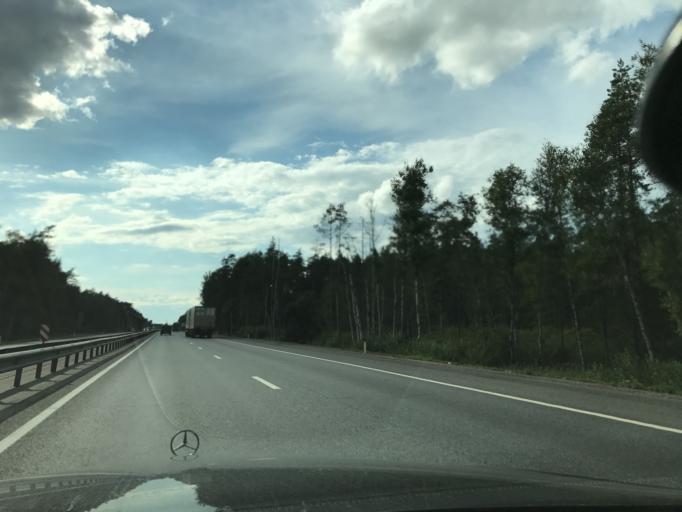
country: RU
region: Moskovskaya
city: Pavlovskiy Posad
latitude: 55.8486
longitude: 38.6897
